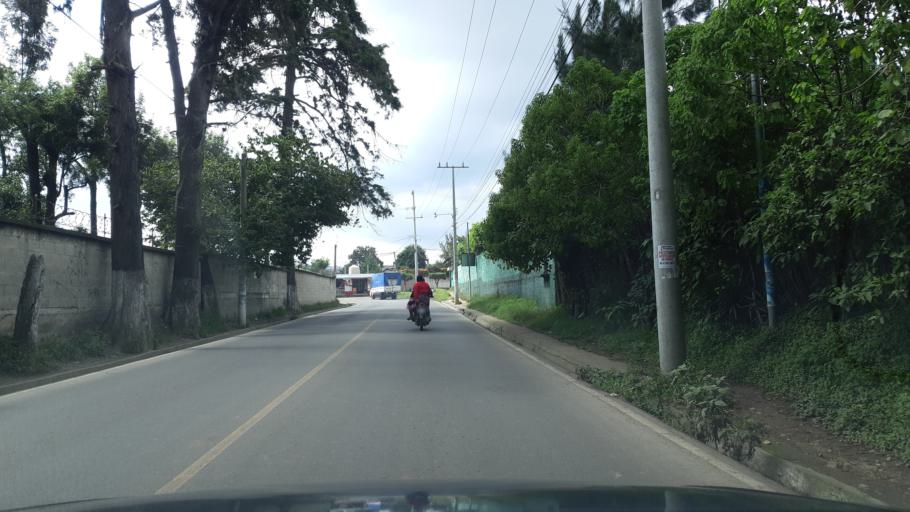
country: GT
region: Chimaltenango
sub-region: Municipio de Chimaltenango
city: Chimaltenango
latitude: 14.6620
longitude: -90.8101
